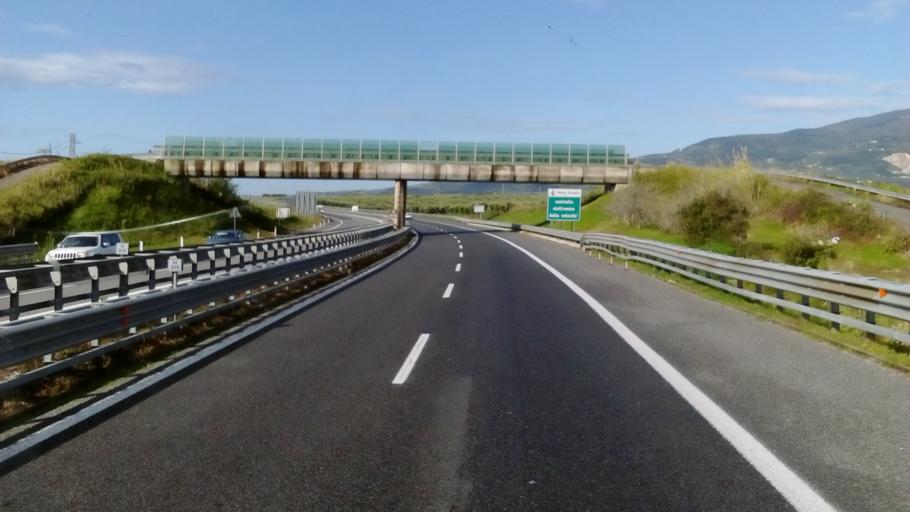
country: IT
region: Calabria
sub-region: Provincia di Catanzaro
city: Santa Eufemia Lamezia
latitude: 38.9225
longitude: 16.2608
